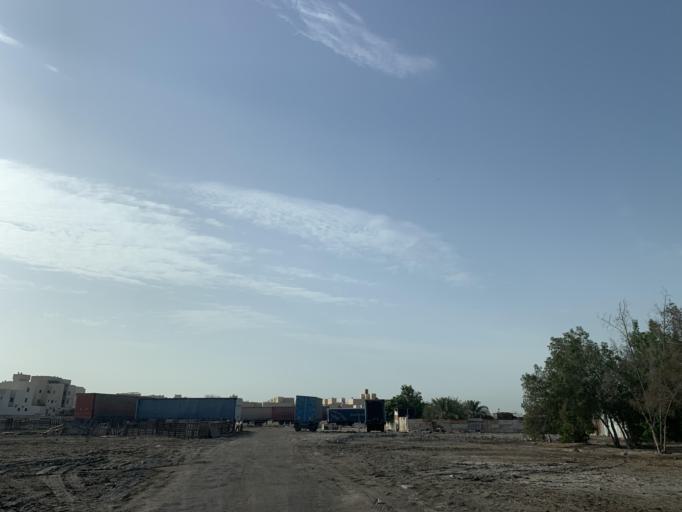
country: BH
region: Manama
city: Manama
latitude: 26.1818
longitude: 50.5872
